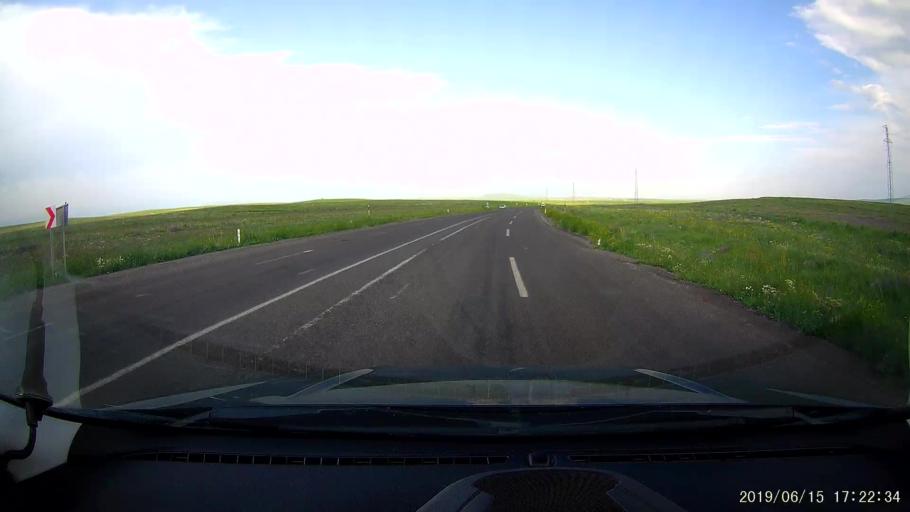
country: TR
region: Kars
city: Basgedikler
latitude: 40.6196
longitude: 43.3458
